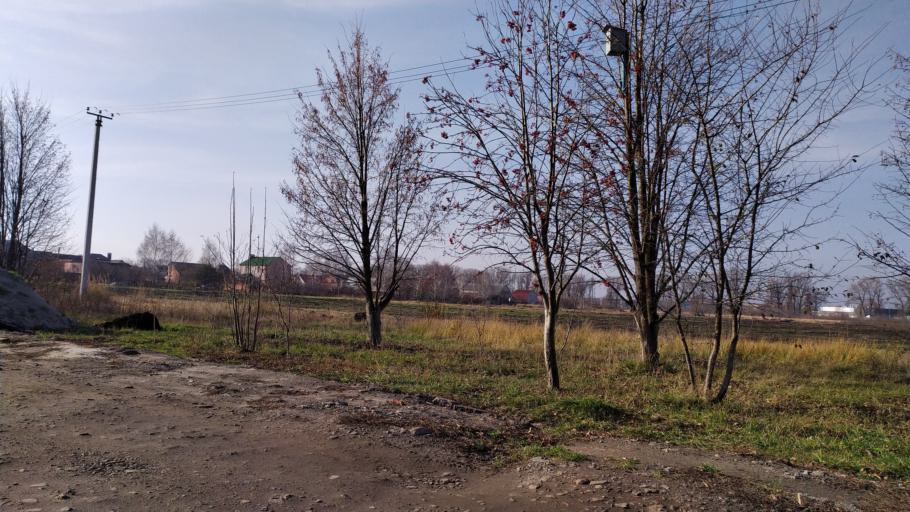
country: RU
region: Kursk
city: Voroshnevo
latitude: 51.6395
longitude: 36.1298
